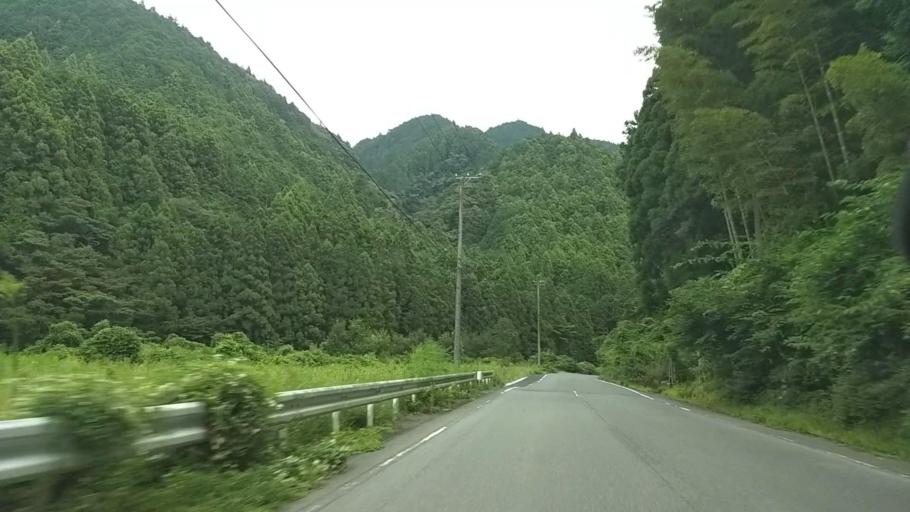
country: JP
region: Shizuoka
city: Fujinomiya
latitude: 35.1611
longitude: 138.5400
